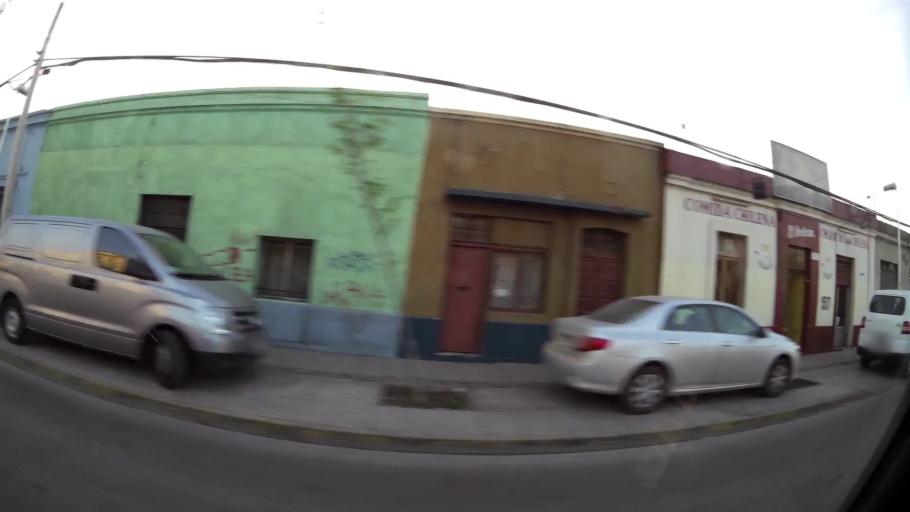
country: CL
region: Santiago Metropolitan
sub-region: Provincia de Santiago
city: Santiago
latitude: -33.4674
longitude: -70.6718
